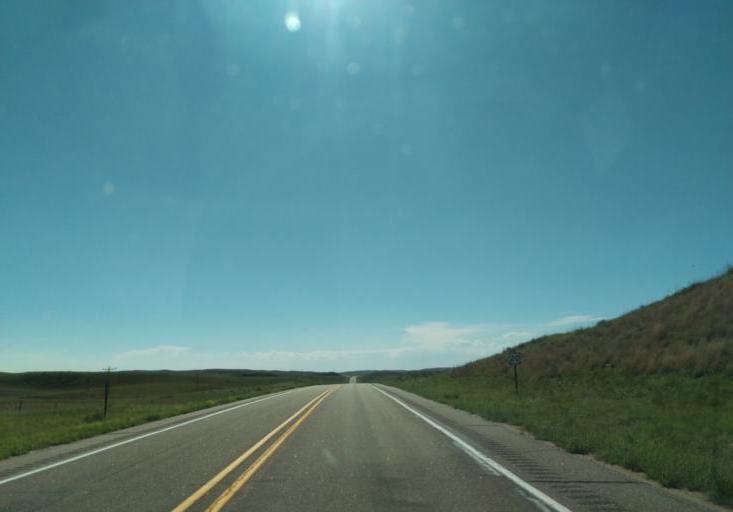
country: US
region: South Dakota
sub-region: Bennett County
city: Martin
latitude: 42.9222
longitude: -101.5218
